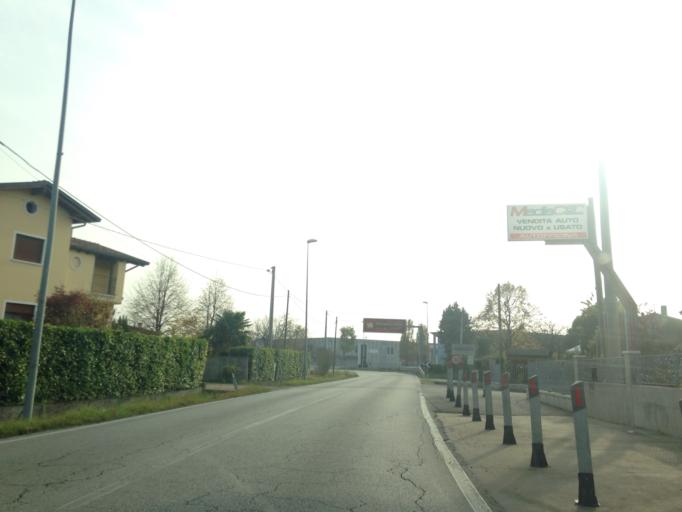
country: IT
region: Friuli Venezia Giulia
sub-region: Provincia di Pordenone
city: Cavolano-Schiavoi
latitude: 45.9236
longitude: 12.5019
